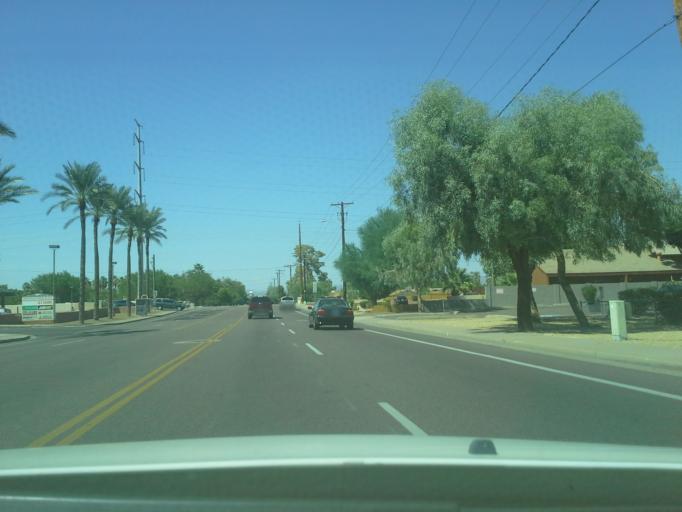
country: US
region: Arizona
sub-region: Maricopa County
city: Phoenix
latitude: 33.3784
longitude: -112.0646
